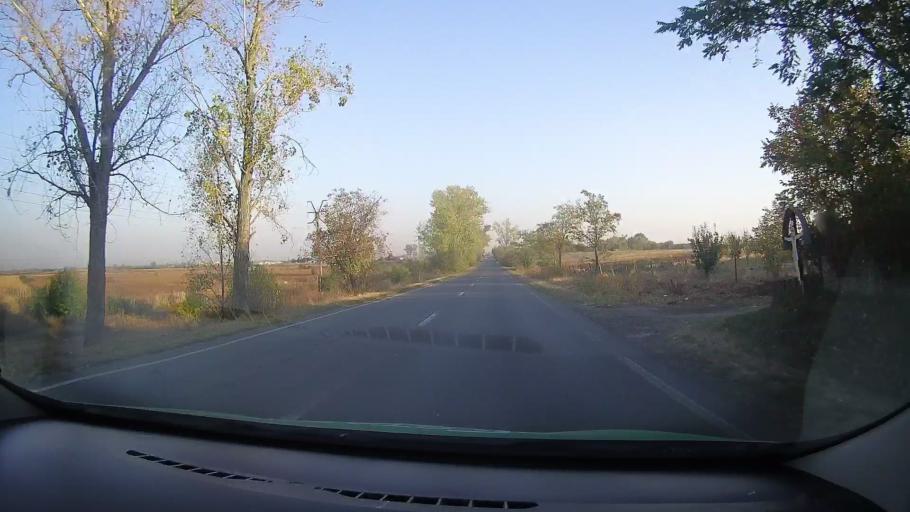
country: RO
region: Arad
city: Arad
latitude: 46.2224
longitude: 21.3205
